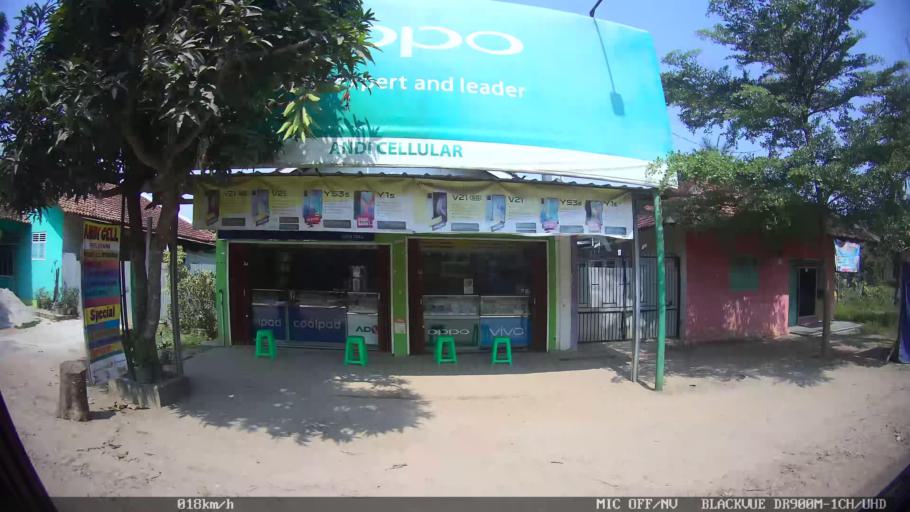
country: ID
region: Lampung
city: Natar
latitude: -5.3086
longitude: 105.2139
